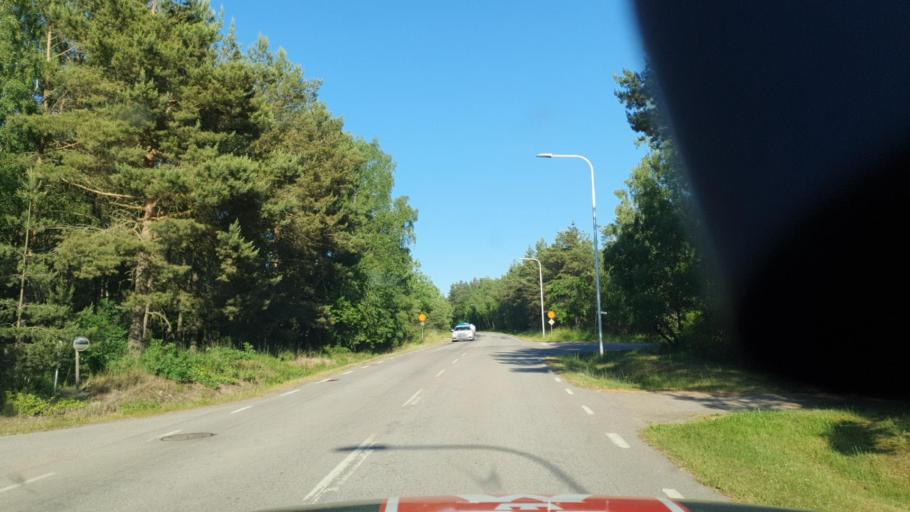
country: SE
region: Kalmar
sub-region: Kalmar Kommun
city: Ljungbyholm
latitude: 56.5918
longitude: 16.1529
